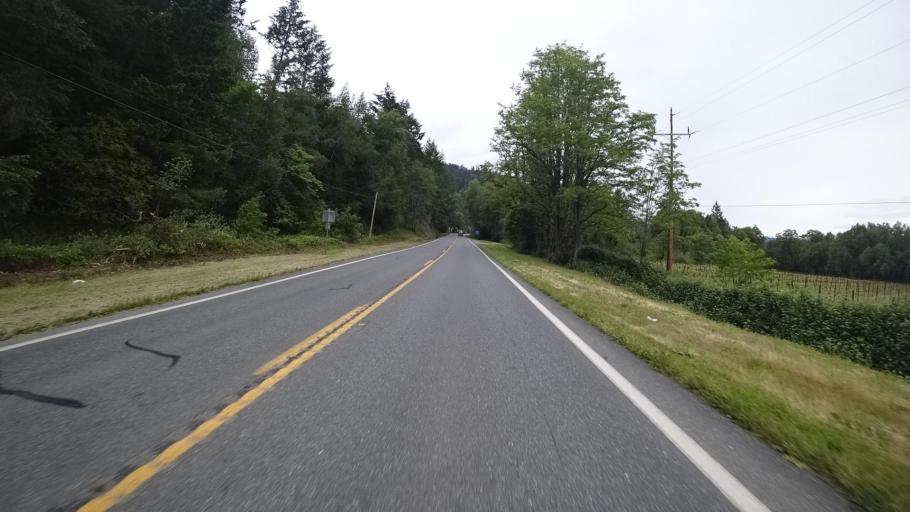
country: US
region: California
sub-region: Humboldt County
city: Willow Creek
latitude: 40.9525
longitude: -123.6408
